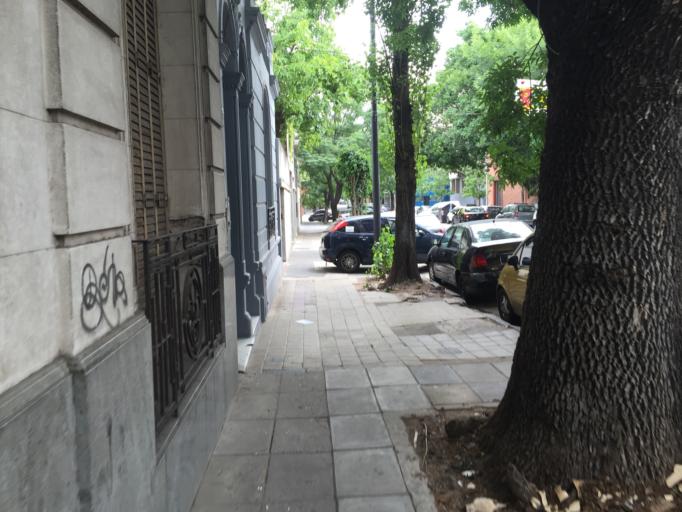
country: AR
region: Buenos Aires F.D.
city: Colegiales
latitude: -34.5863
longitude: -58.4428
